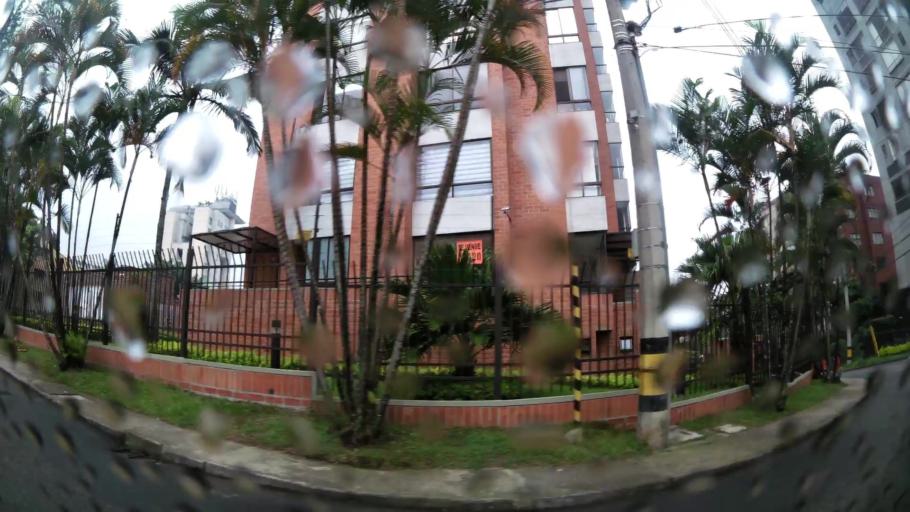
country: CO
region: Antioquia
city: Envigado
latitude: 6.1994
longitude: -75.5676
